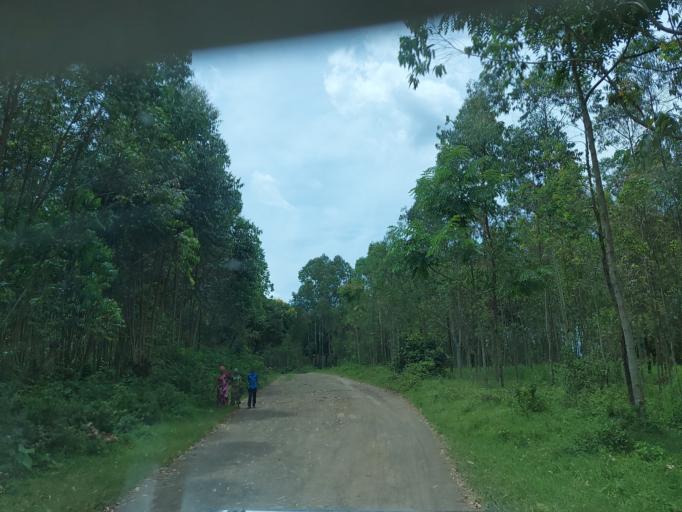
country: CD
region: South Kivu
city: Bukavu
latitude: -2.2462
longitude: 28.8265
